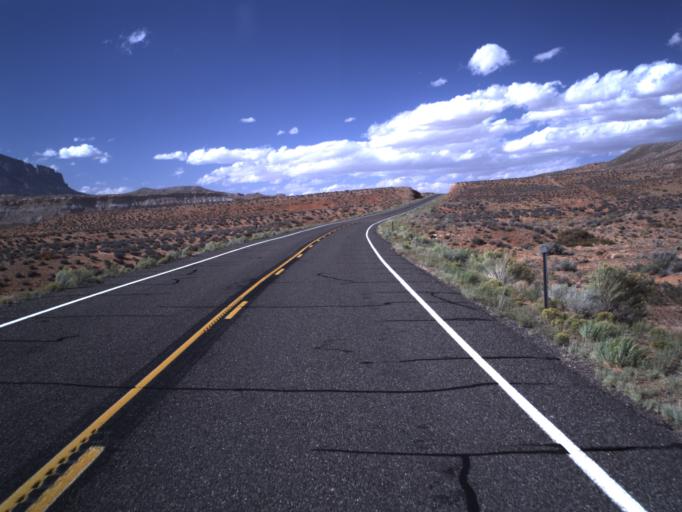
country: US
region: Utah
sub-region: Wayne County
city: Loa
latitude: 38.0691
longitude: -110.6056
